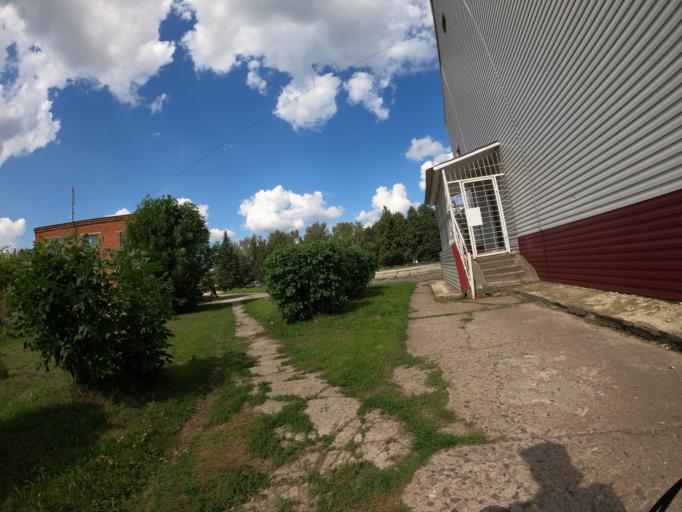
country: RU
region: Moskovskaya
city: Voskresensk
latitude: 55.2756
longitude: 38.6469
